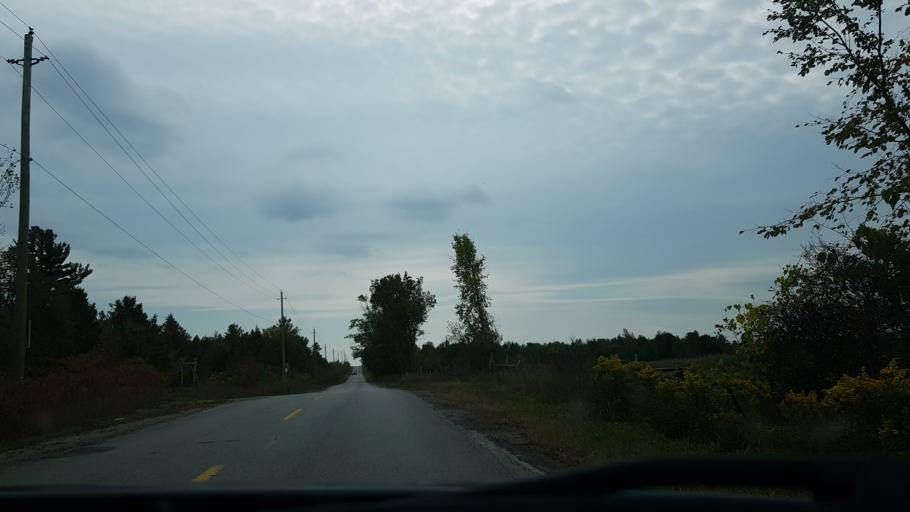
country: CA
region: Ontario
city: Orillia
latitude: 44.6586
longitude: -78.9688
